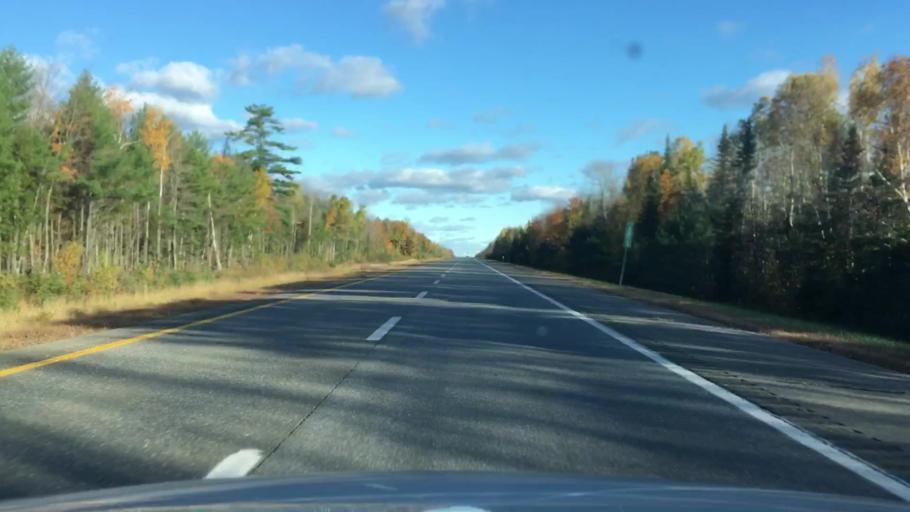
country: US
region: Maine
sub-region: Penobscot County
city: Greenbush
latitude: 45.0732
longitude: -68.6908
